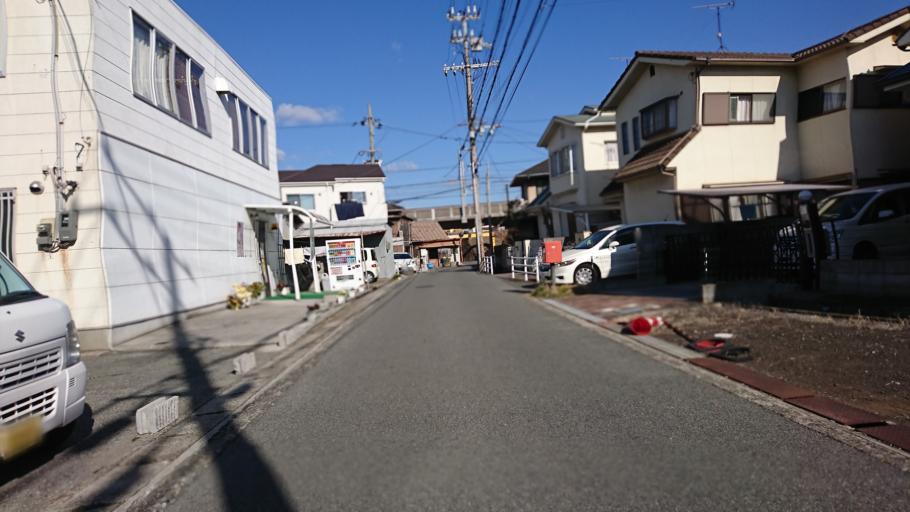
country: JP
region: Hyogo
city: Kakogawacho-honmachi
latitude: 34.7281
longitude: 134.8528
